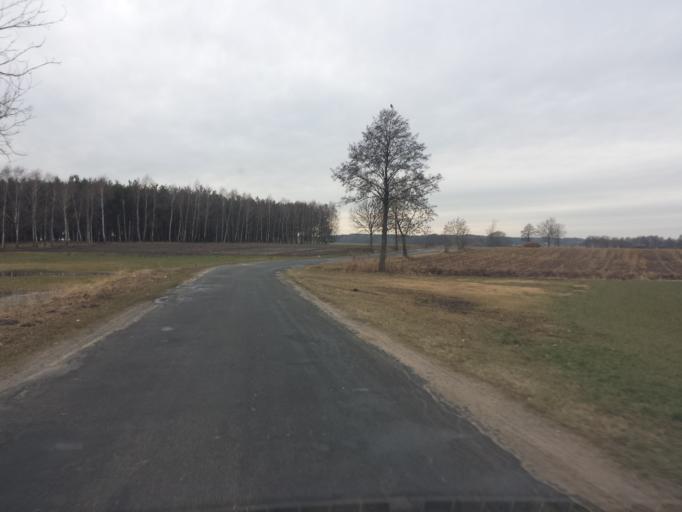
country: PL
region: Lodz Voivodeship
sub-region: Powiat wielunski
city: Osjakow
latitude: 51.2887
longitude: 18.7747
